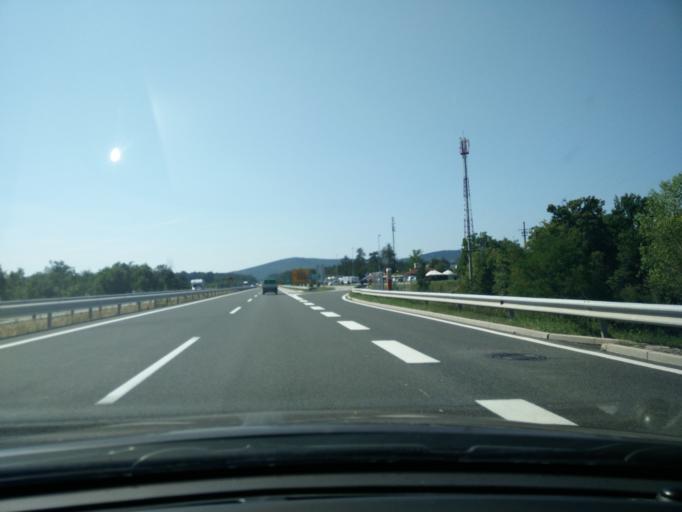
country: SI
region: Divaca
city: Divaca
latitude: 45.6744
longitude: 13.9720
